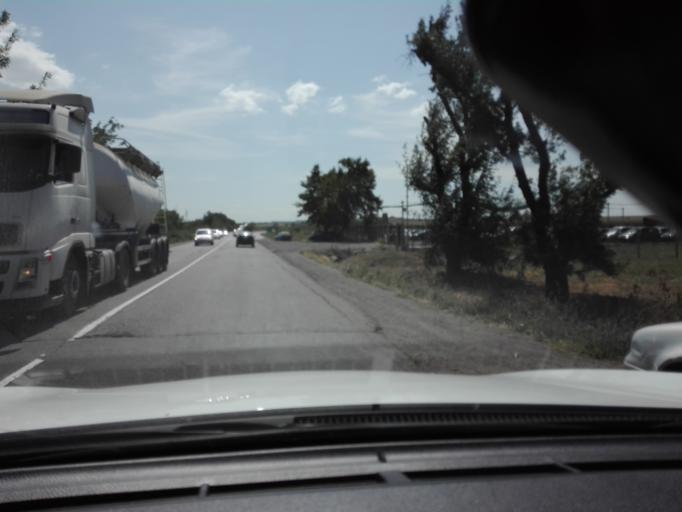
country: BG
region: Burgas
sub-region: Obshtina Kameno
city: Kameno
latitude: 42.5984
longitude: 27.3899
